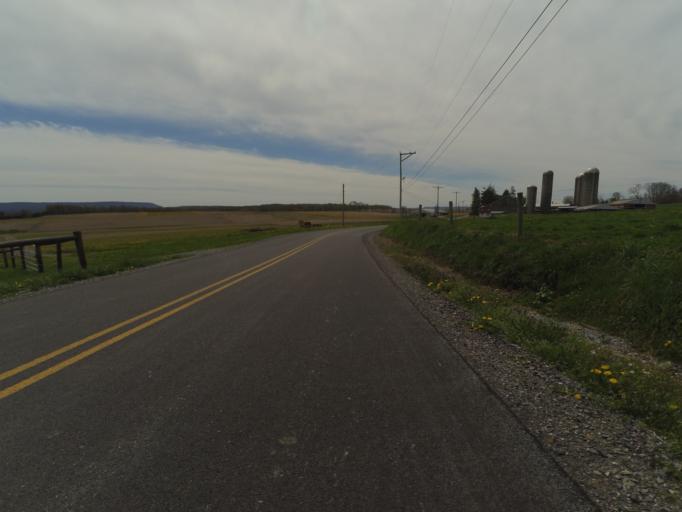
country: US
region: Pennsylvania
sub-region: Blair County
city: Tyrone
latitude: 40.7110
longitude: -78.1471
